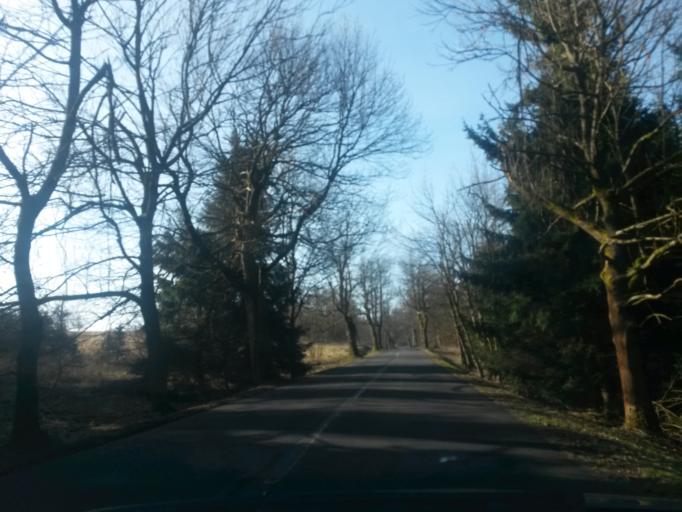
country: CZ
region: Ustecky
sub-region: Okres Chomutov
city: Perstejn
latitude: 50.4400
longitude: 13.1338
